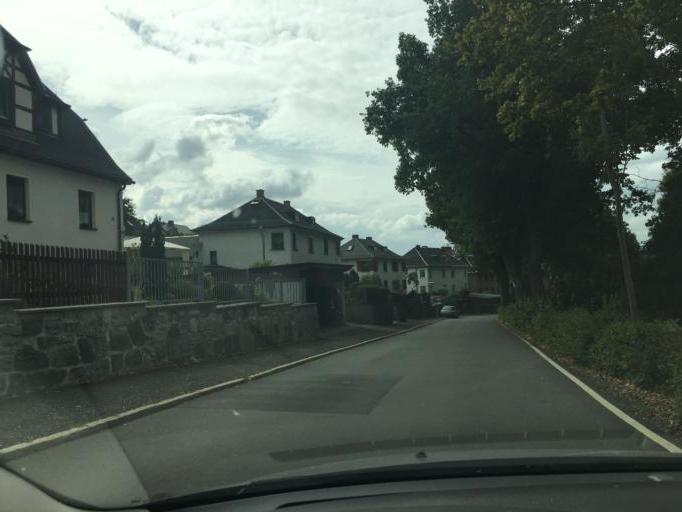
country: DE
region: Thuringia
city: Burgk
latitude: 50.5025
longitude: 11.7362
